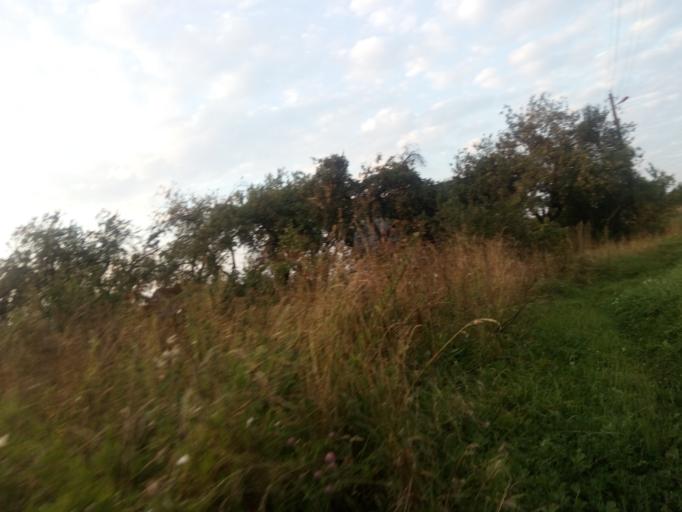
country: BY
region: Vitebsk
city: Dzisna
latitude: 55.6631
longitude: 28.3334
